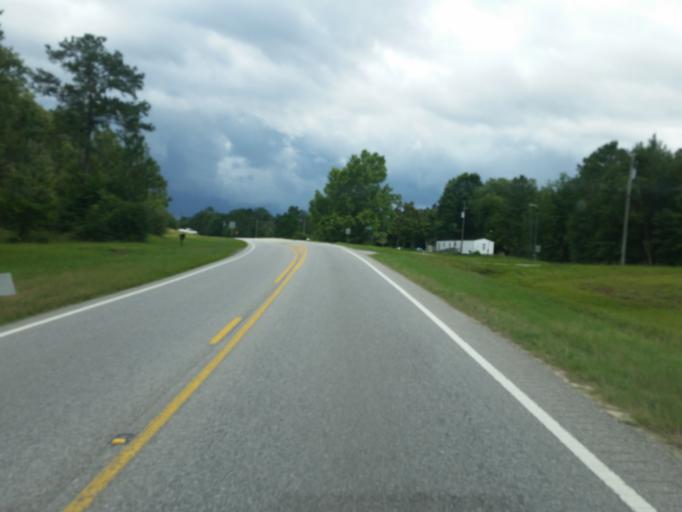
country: US
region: Mississippi
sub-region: George County
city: Lucedale
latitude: 30.8522
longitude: -88.4052
